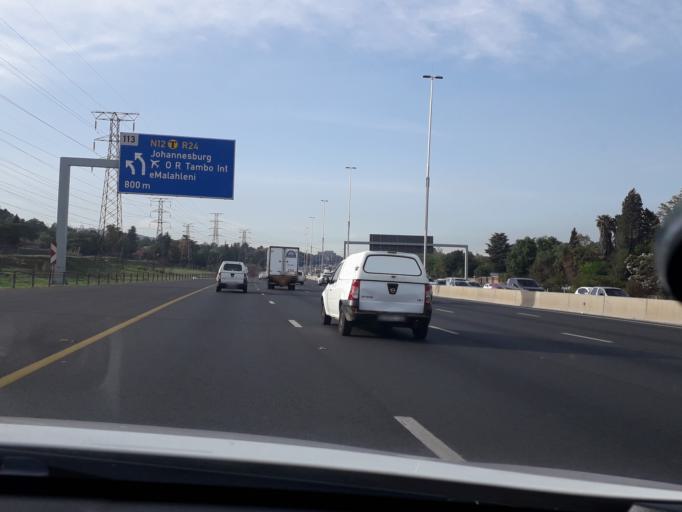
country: ZA
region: Gauteng
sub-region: City of Johannesburg Metropolitan Municipality
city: Modderfontein
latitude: -26.1541
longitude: 28.1327
